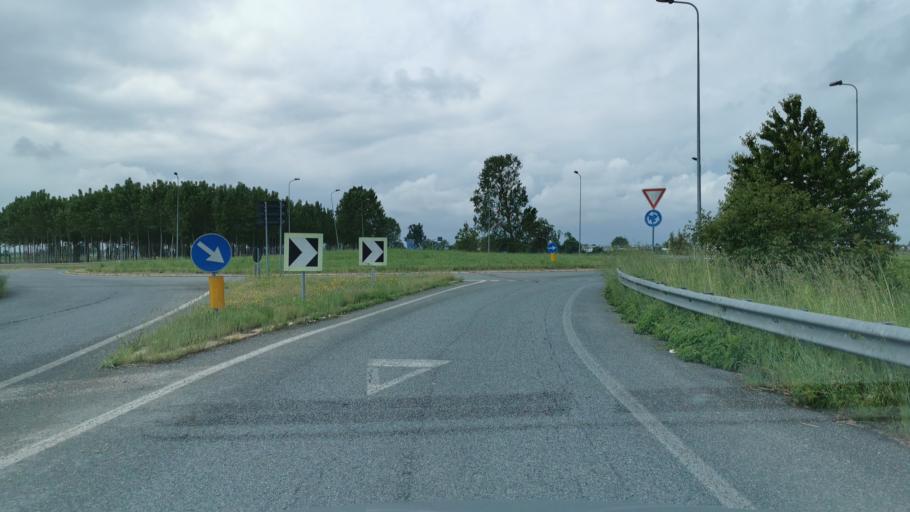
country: IT
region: Piedmont
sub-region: Provincia di Cuneo
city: Racconigi
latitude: 44.7494
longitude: 7.6911
